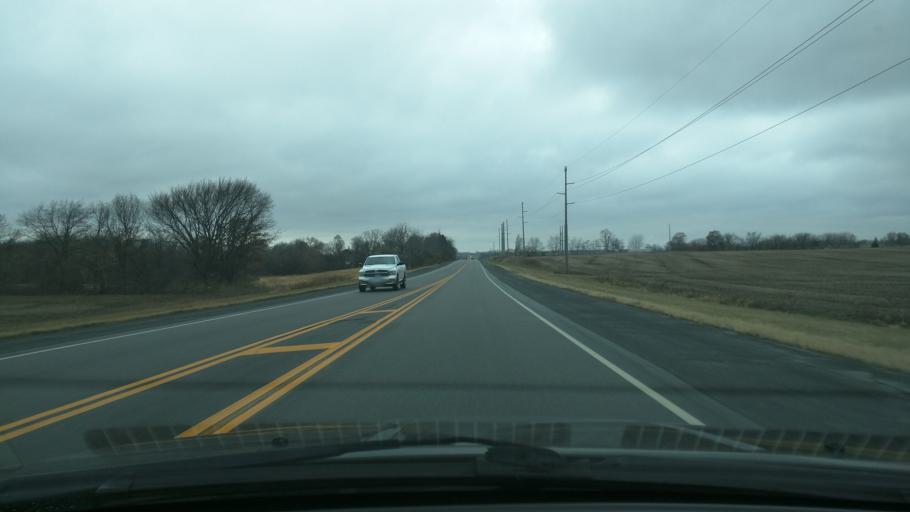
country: US
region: Minnesota
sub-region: Dakota County
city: Hastings
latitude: 44.7384
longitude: -92.9077
